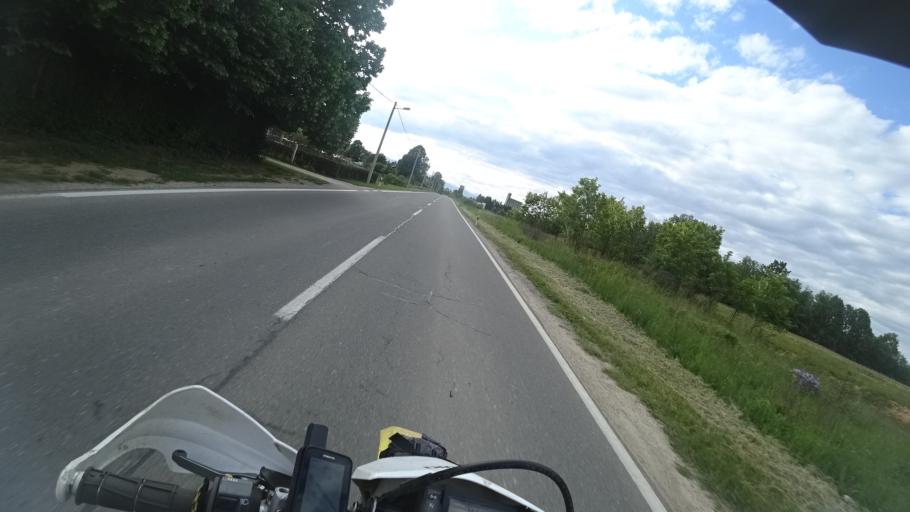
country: HR
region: Licko-Senjska
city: Gospic
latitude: 44.5289
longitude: 15.4053
